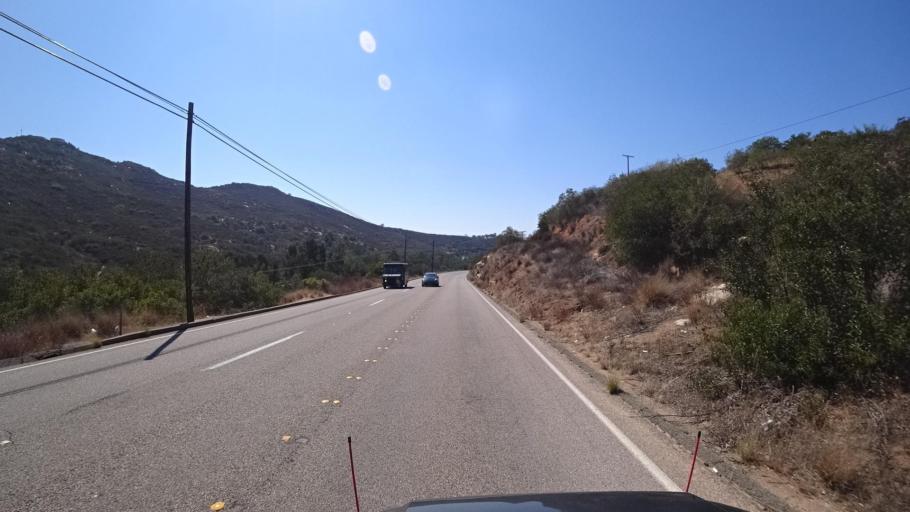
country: US
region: California
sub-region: San Diego County
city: Crest
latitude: 32.8114
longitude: -116.8771
